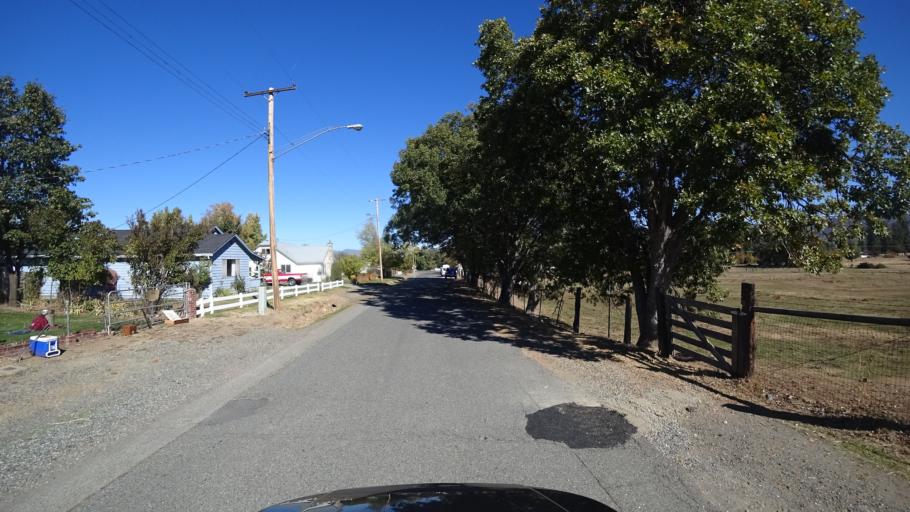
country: US
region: California
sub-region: Siskiyou County
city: Yreka
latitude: 41.4599
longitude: -122.8894
